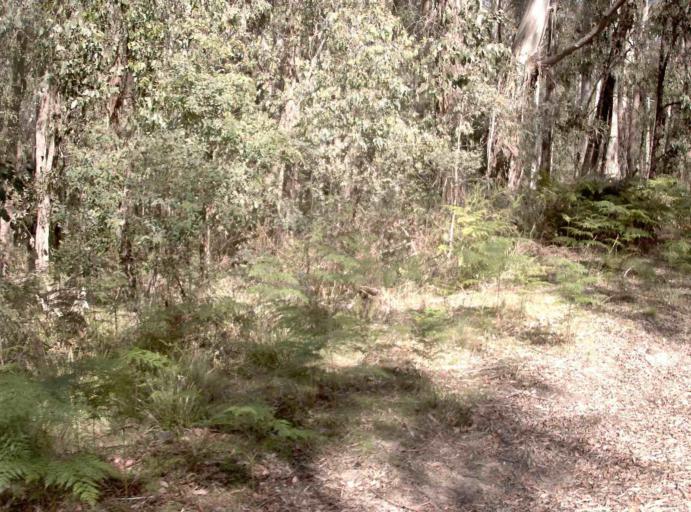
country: AU
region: New South Wales
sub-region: Bombala
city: Bombala
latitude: -37.1240
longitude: 148.7506
